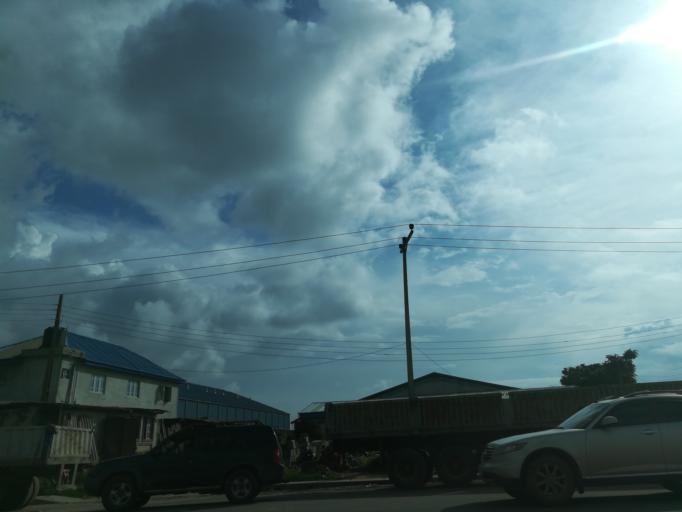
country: NG
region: Lagos
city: Ebute Ikorodu
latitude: 6.5943
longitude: 3.5055
